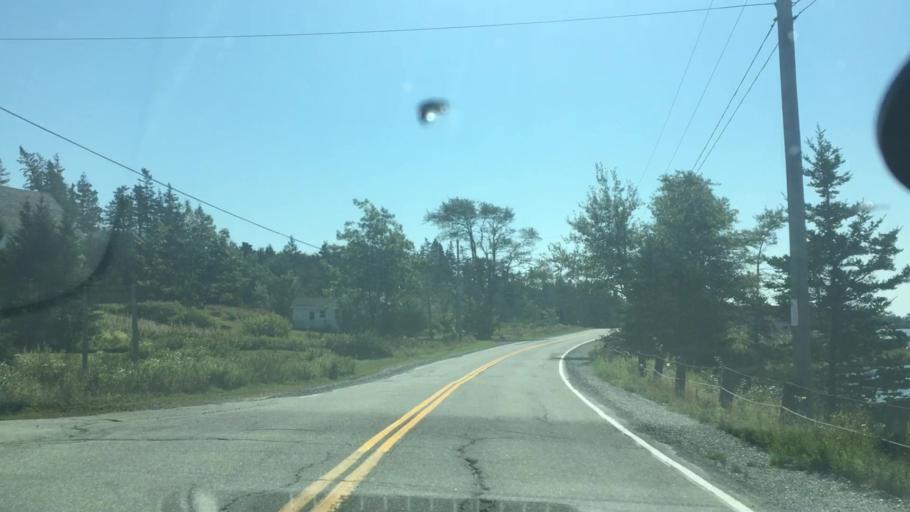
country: CA
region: Nova Scotia
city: New Glasgow
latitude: 44.9156
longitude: -62.3817
